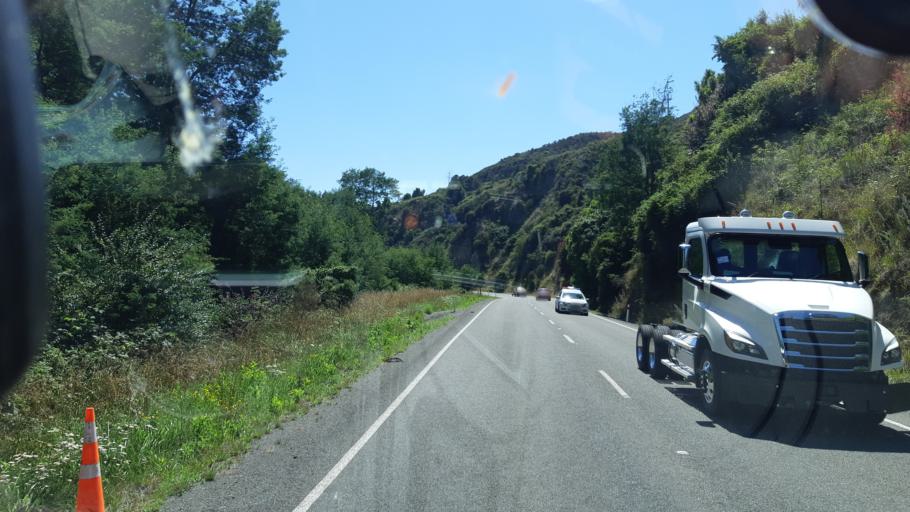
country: NZ
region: Canterbury
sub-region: Kaikoura District
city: Kaikoura
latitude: -42.6325
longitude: 173.3528
